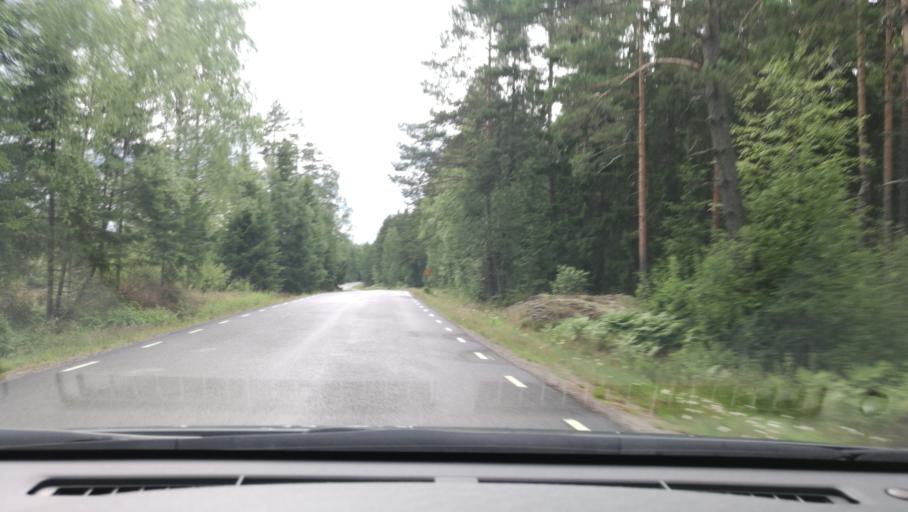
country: SE
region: OEstergoetland
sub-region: Norrkopings Kommun
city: Svartinge
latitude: 58.8196
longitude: 16.0694
